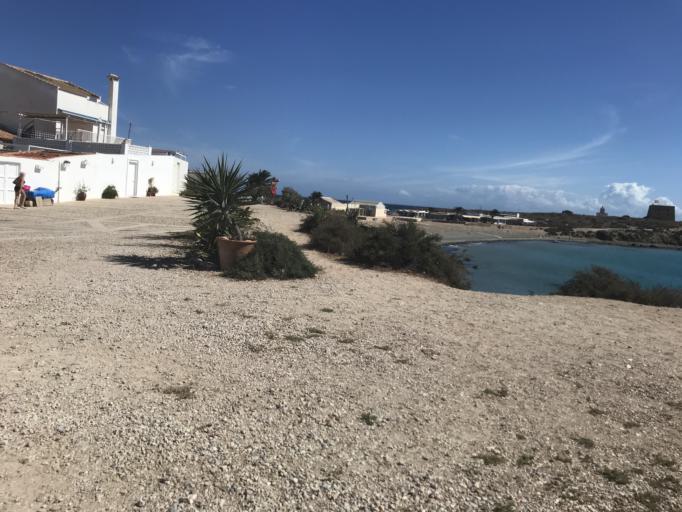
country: ES
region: Valencia
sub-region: Provincia de Alicante
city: Santa Pola
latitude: 38.1657
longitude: -0.4809
